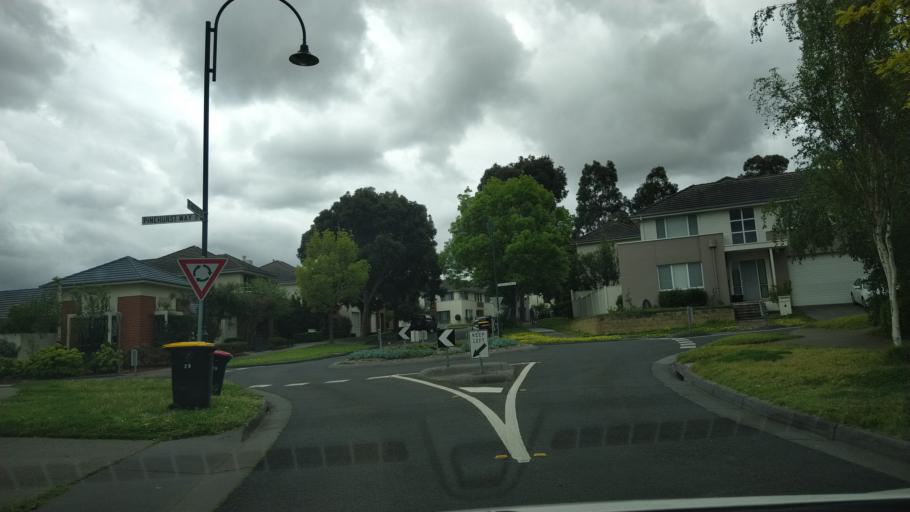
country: AU
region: Victoria
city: Heatherton
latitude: -37.9563
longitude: 145.0821
